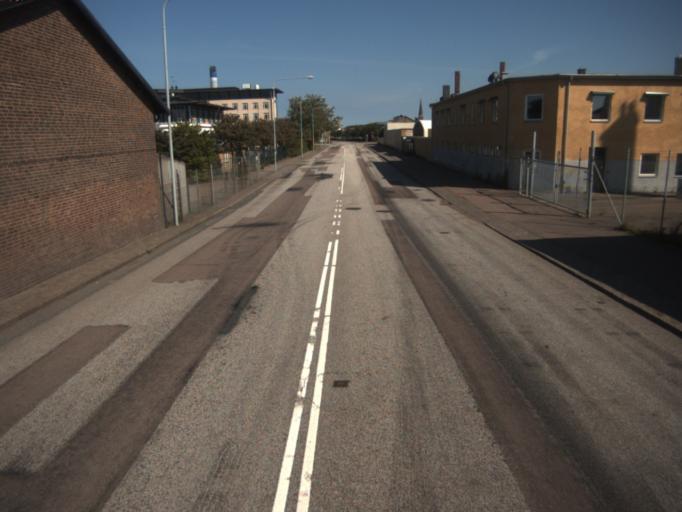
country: SE
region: Skane
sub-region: Helsingborg
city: Helsingborg
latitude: 56.0304
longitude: 12.7058
